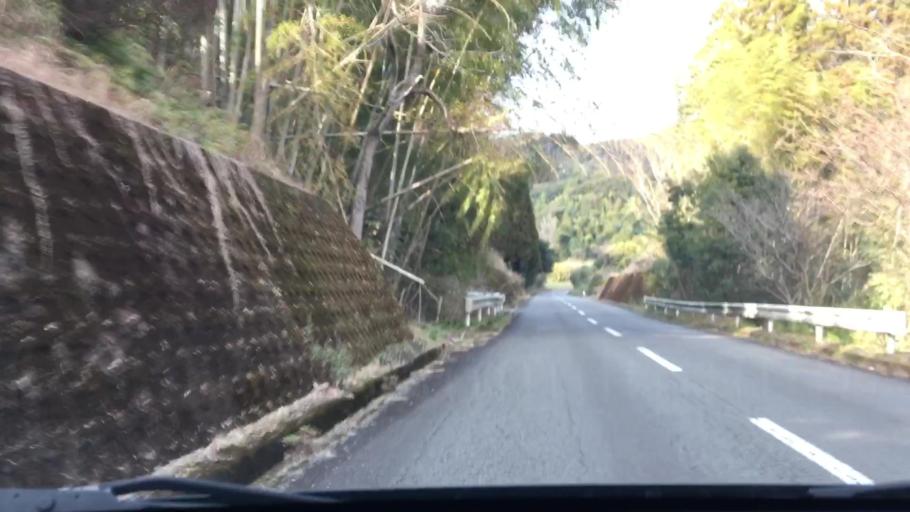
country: JP
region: Miyazaki
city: Nichinan
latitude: 31.5932
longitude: 131.3071
